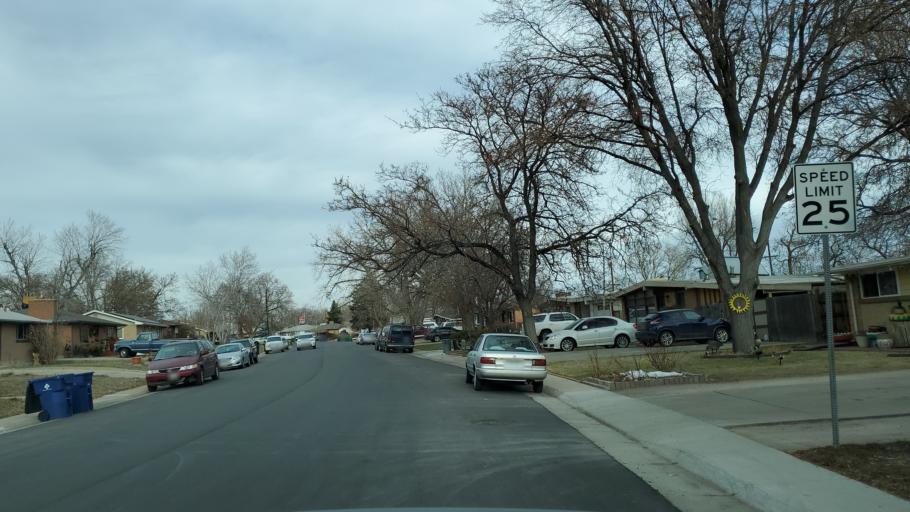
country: US
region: Colorado
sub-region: Adams County
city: Westminster
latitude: 39.8387
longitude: -105.0266
